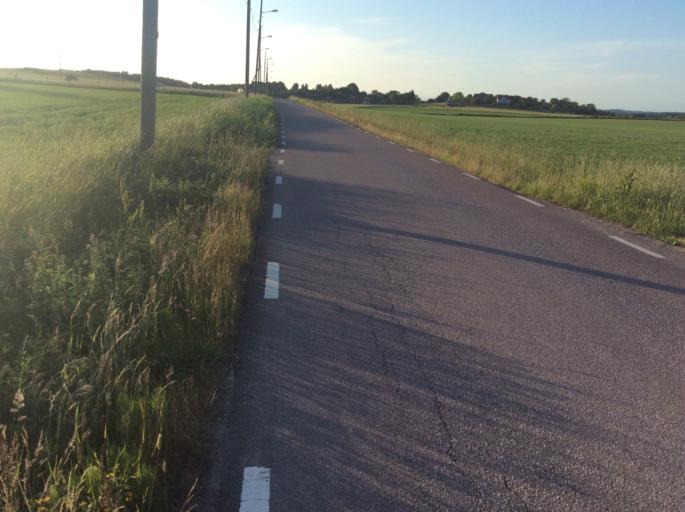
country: SE
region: Vaestra Goetaland
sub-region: Goteborg
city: Majorna
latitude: 57.7934
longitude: 11.8877
